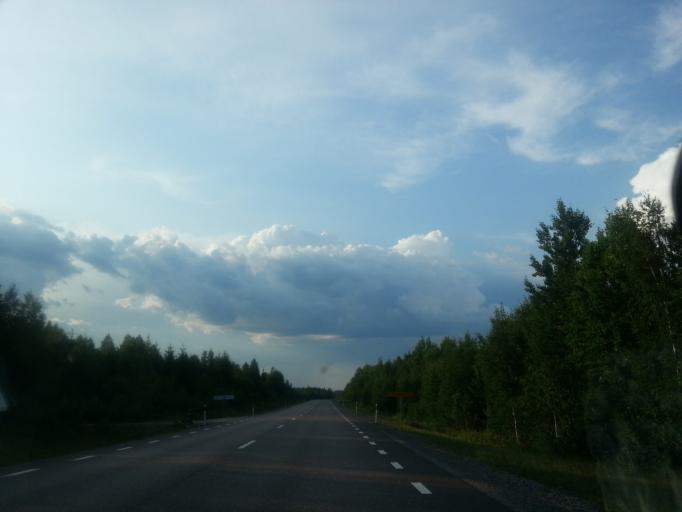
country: SE
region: Dalarna
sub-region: Avesta Kommun
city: Horndal
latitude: 60.3317
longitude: 16.4121
